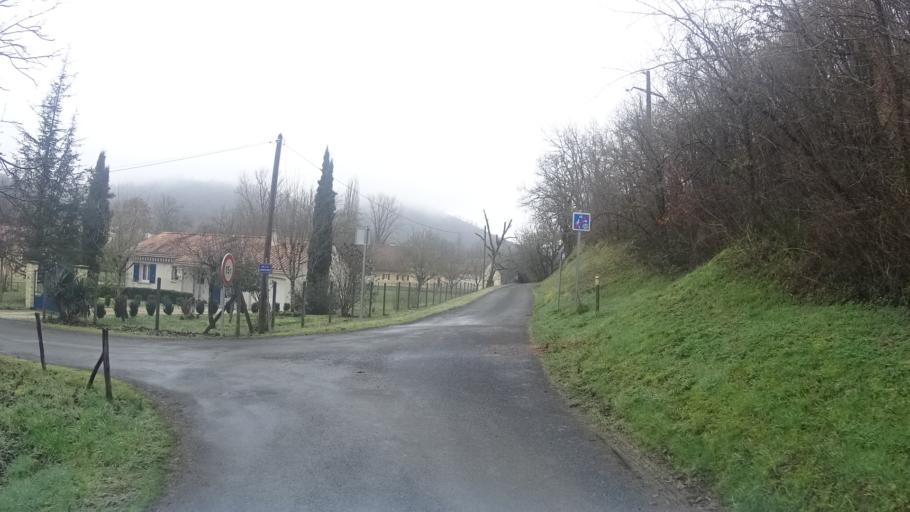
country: FR
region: Aquitaine
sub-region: Departement de la Dordogne
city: Terrasson-Lavilledieu
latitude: 45.1144
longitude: 1.2338
